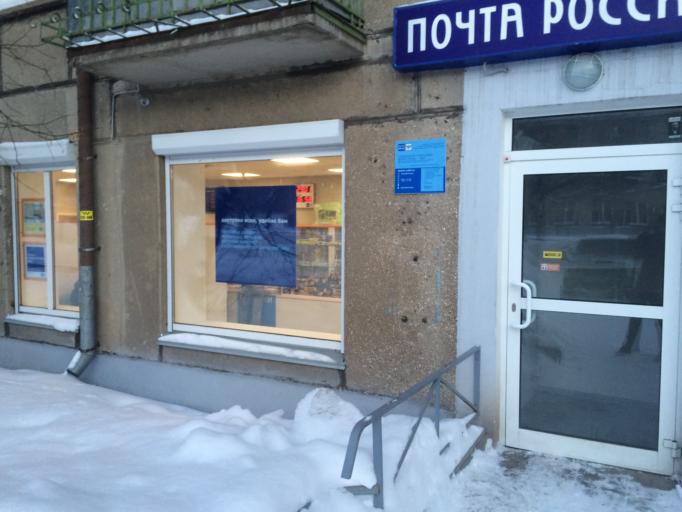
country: RU
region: Chelyabinsk
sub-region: Gorod Magnitogorsk
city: Magnitogorsk
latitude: 53.4057
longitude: 58.9717
